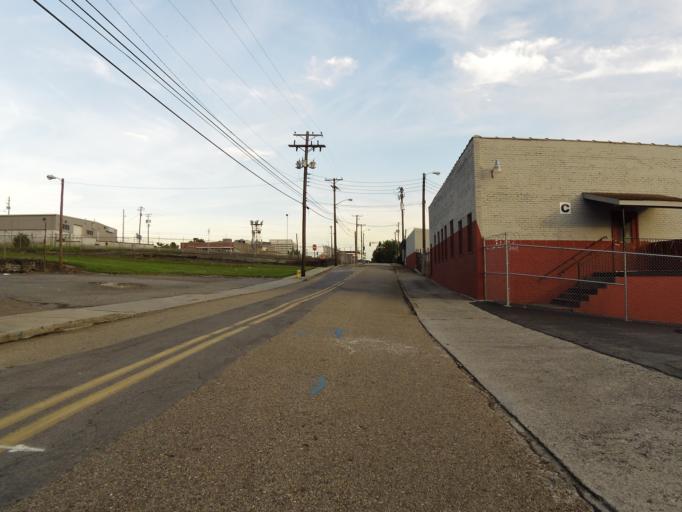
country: US
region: Tennessee
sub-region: Knox County
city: Knoxville
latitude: 35.9731
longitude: -83.9270
